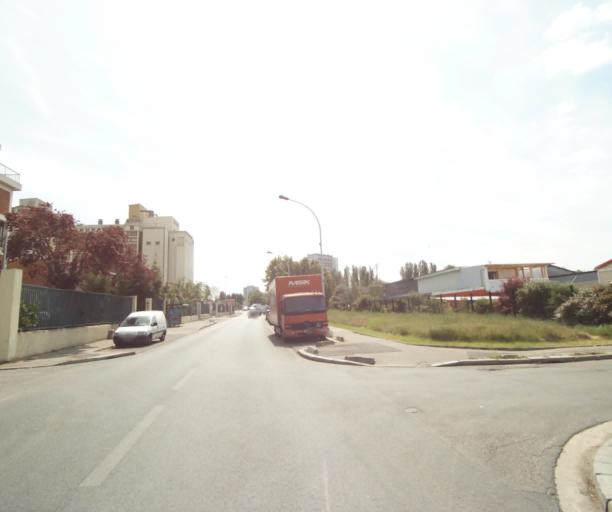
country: FR
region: Ile-de-France
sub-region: Departement des Hauts-de-Seine
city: Villeneuve-la-Garenne
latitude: 48.9222
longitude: 2.3235
